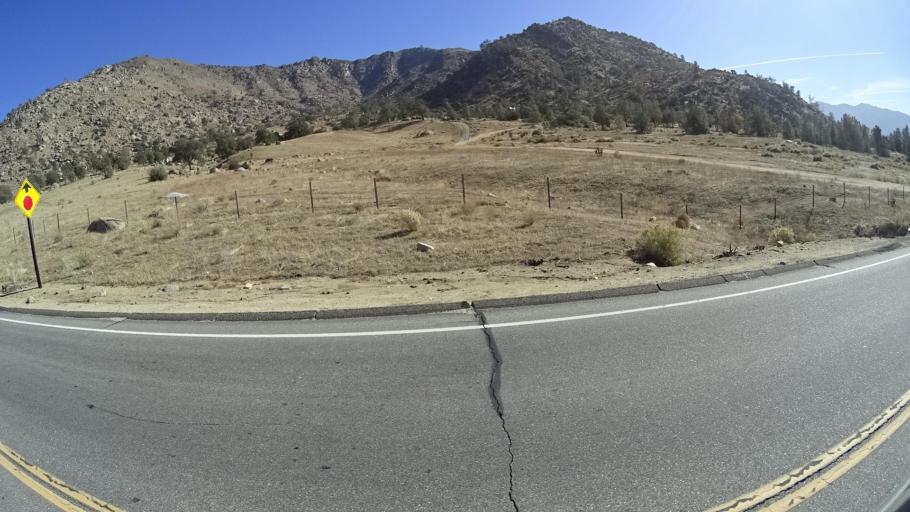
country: US
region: California
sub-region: Kern County
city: Lake Isabella
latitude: 35.6412
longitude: -118.4634
